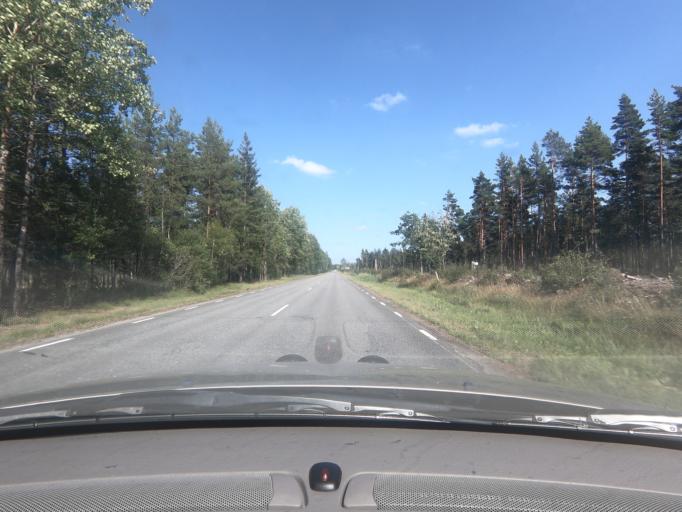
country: SE
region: Joenkoeping
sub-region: Vetlanda Kommun
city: Landsbro
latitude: 57.3797
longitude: 14.9423
